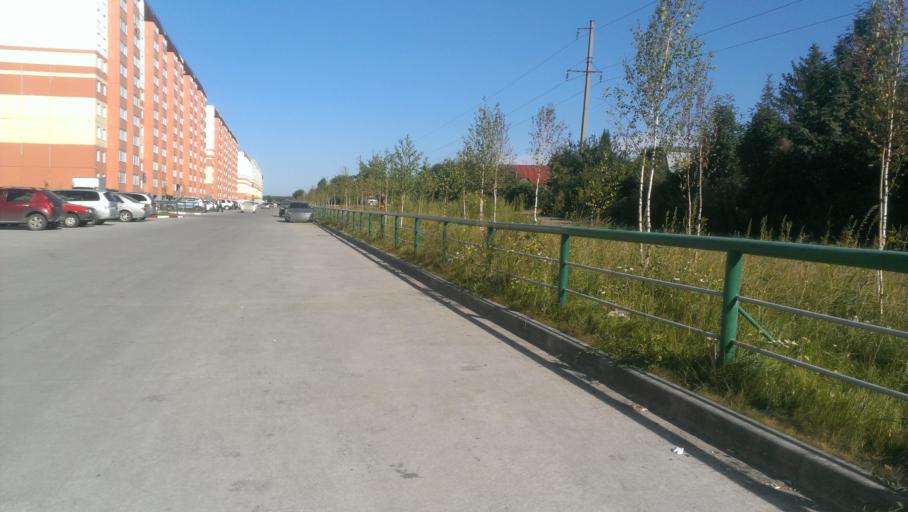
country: RU
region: Altai Krai
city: Novosilikatnyy
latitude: 53.3259
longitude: 83.6687
